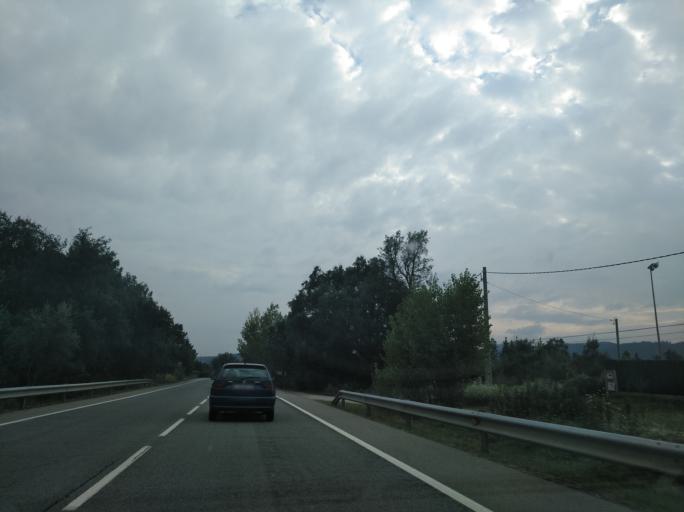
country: ES
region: Catalonia
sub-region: Provincia de Girona
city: Santa Coloma de Farners
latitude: 41.8830
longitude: 2.6581
